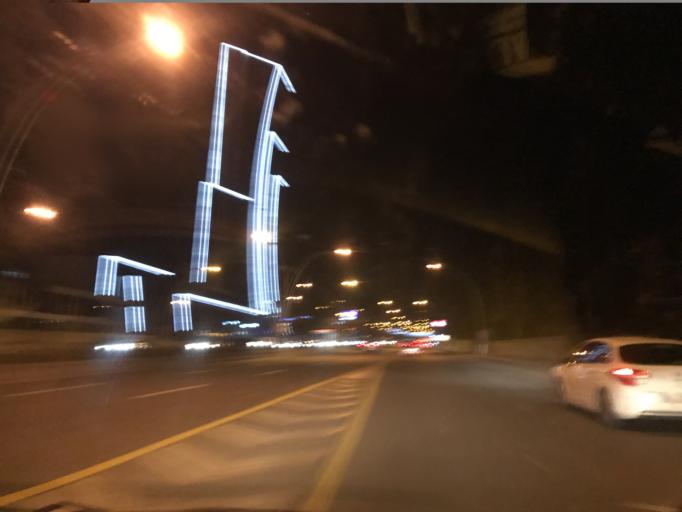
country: TR
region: Ankara
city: Ankara
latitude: 39.8845
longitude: 32.8120
